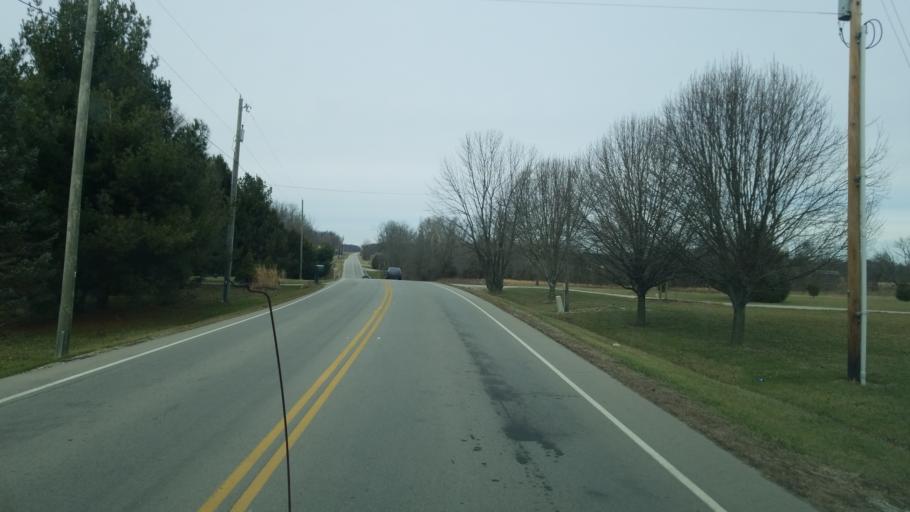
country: US
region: Ohio
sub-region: Adams County
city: Winchester
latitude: 39.0363
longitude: -83.7042
